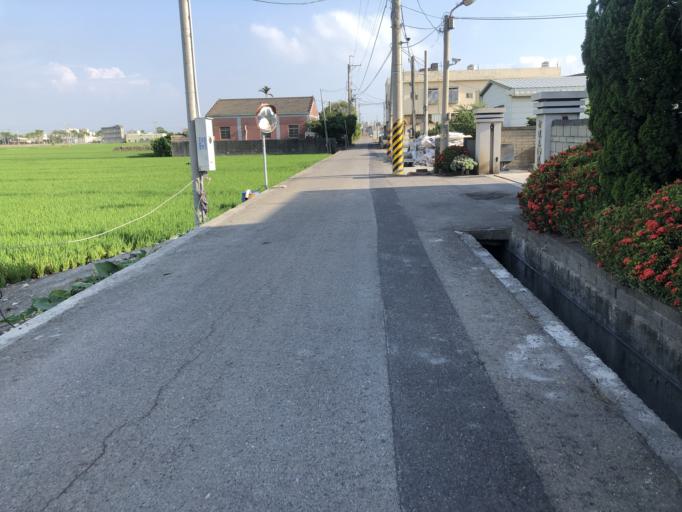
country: TW
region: Taiwan
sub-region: Changhua
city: Chang-hua
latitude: 24.0542
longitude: 120.4672
